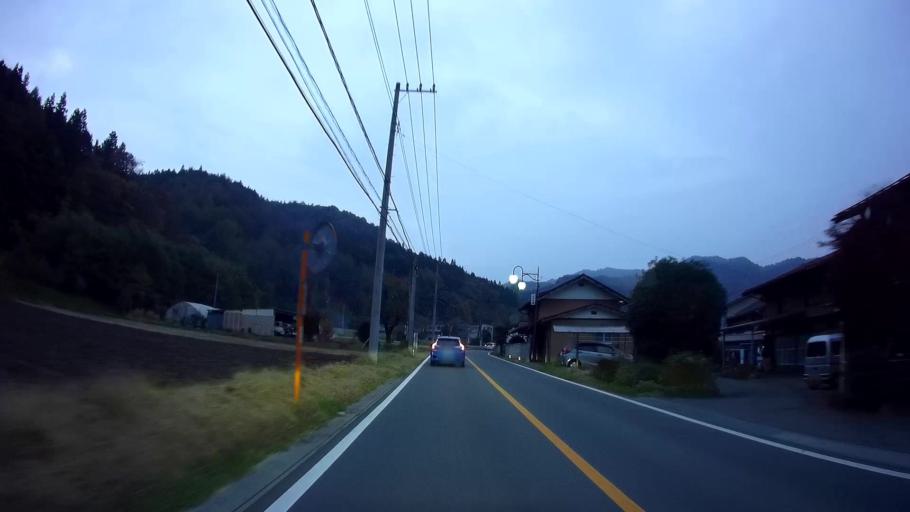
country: JP
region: Gunma
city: Nakanojomachi
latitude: 36.5342
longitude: 138.7845
